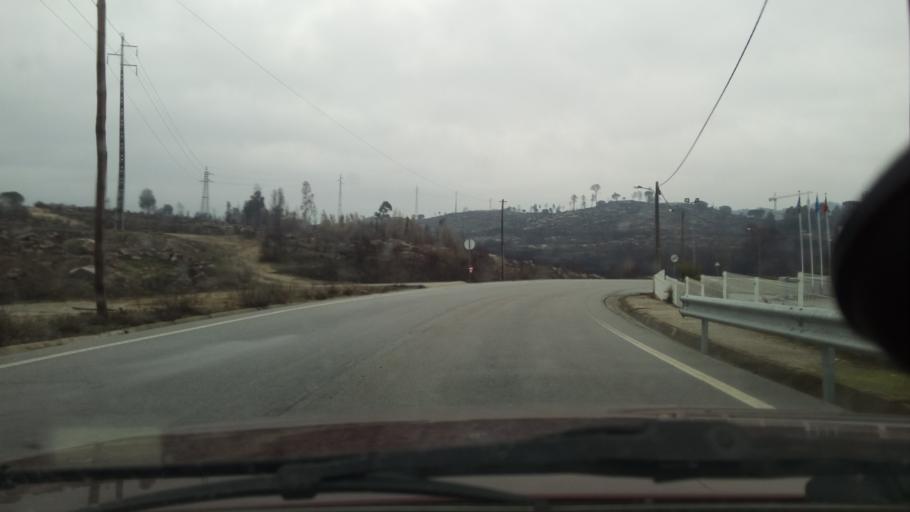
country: PT
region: Viseu
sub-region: Mangualde
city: Mangualde
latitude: 40.6020
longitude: -7.8004
